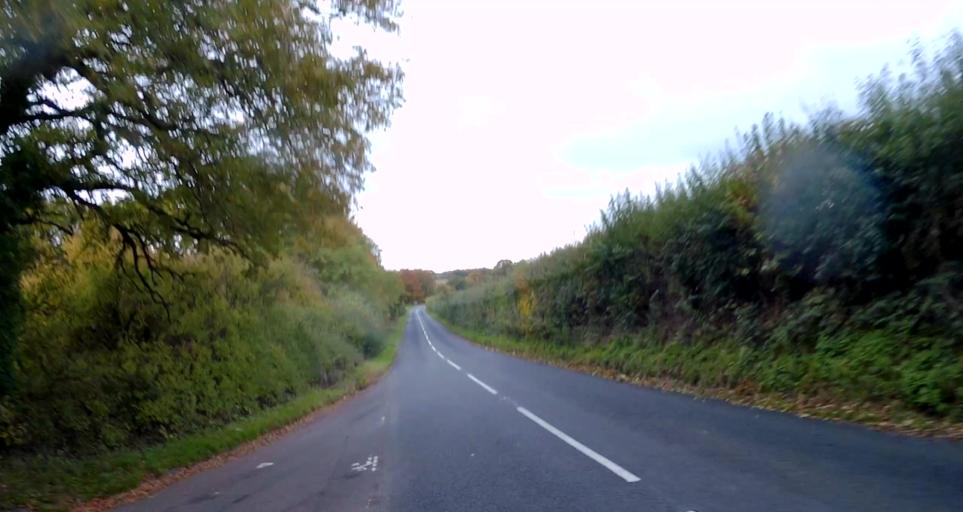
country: GB
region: England
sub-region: Hampshire
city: Four Marks
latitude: 51.1169
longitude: -1.1565
